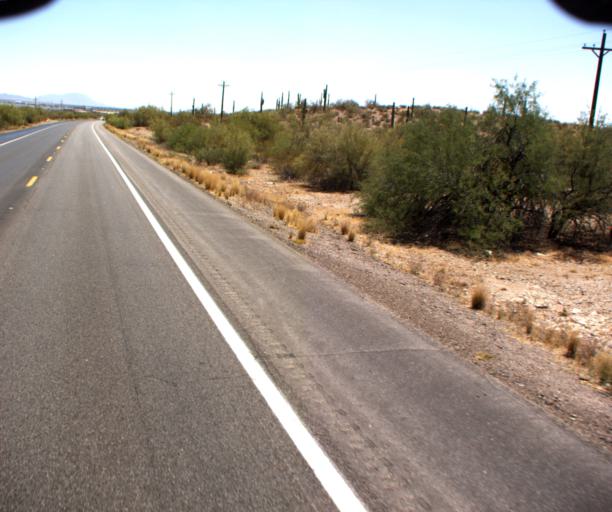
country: US
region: Arizona
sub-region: Pinal County
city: Florence
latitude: 33.0832
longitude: -111.3742
